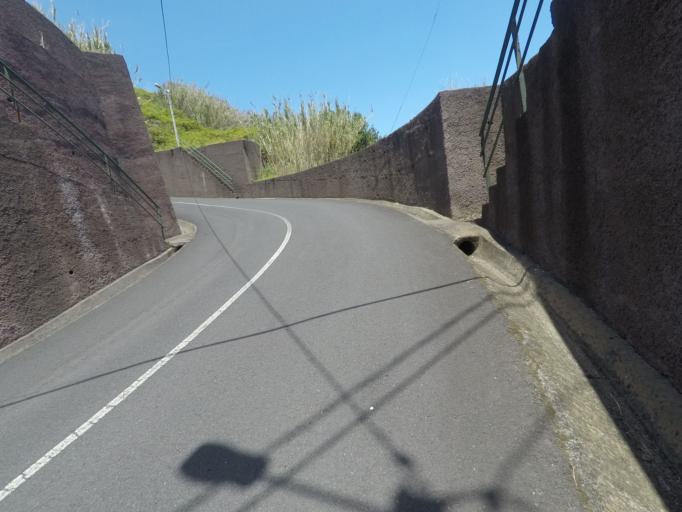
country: PT
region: Madeira
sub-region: Porto Moniz
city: Porto Moniz
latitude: 32.8310
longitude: -17.1322
